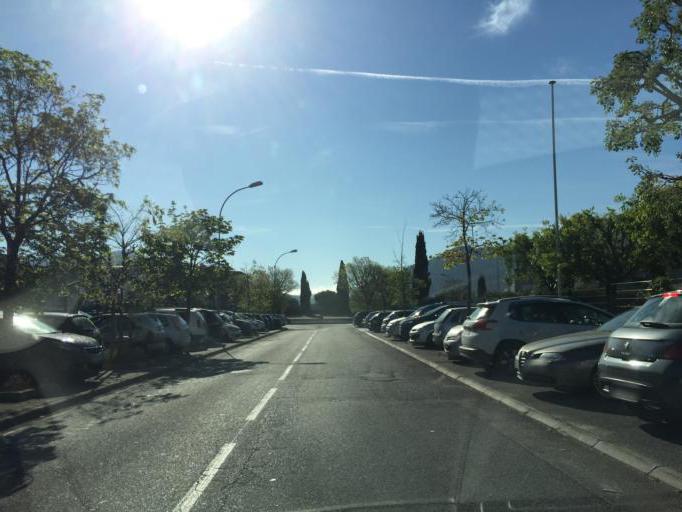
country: FR
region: Provence-Alpes-Cote d'Azur
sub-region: Departement des Bouches-du-Rhone
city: Gemenos
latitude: 43.2868
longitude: 5.6056
